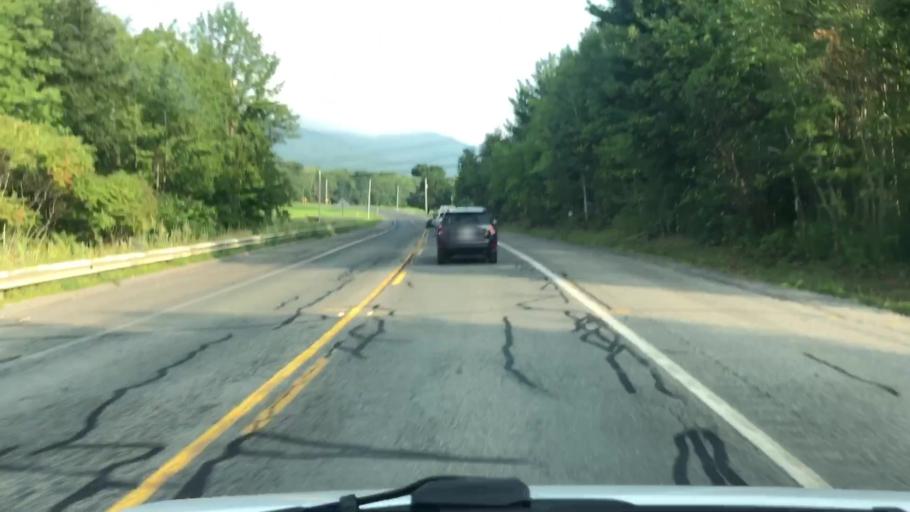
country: US
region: Massachusetts
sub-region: Berkshire County
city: Williamstown
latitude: 42.6404
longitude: -73.2289
